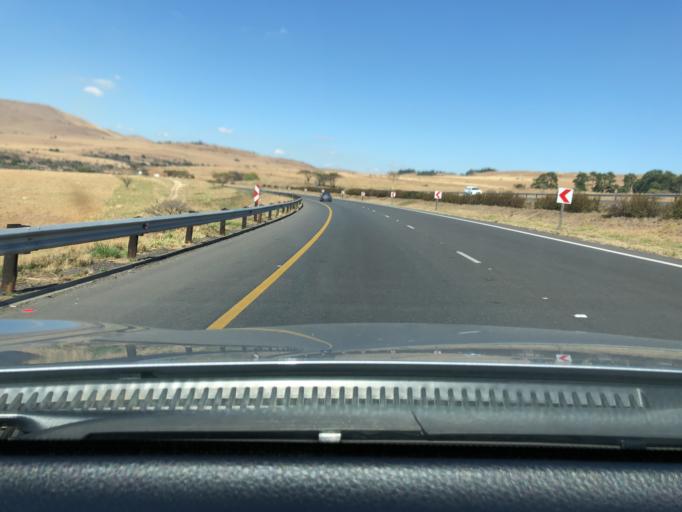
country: ZA
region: KwaZulu-Natal
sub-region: uThukela District Municipality
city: Estcourt
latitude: -29.0773
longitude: 29.9175
